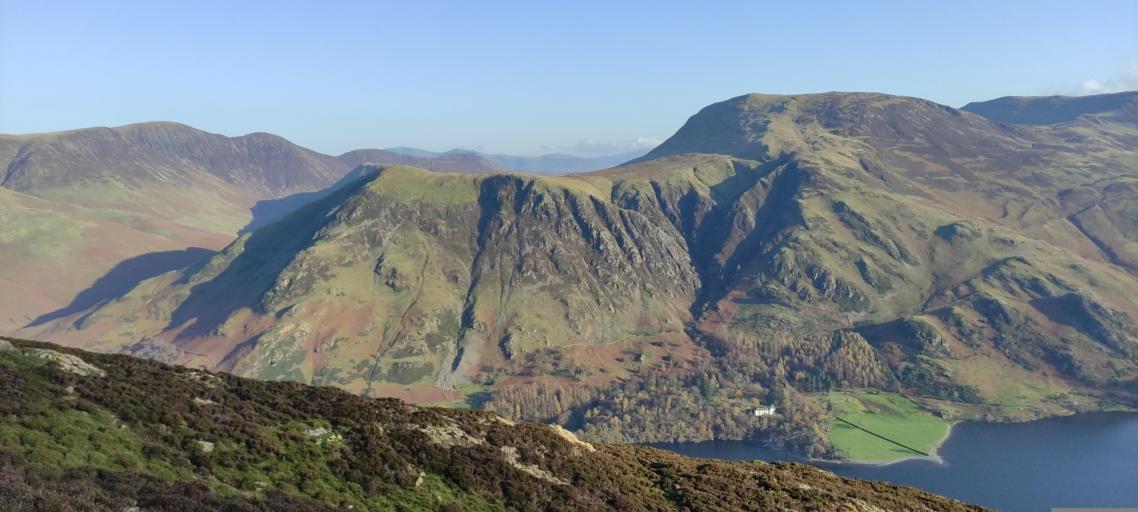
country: GB
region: England
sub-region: Cumbria
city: Keswick
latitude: 54.5246
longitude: -3.2743
